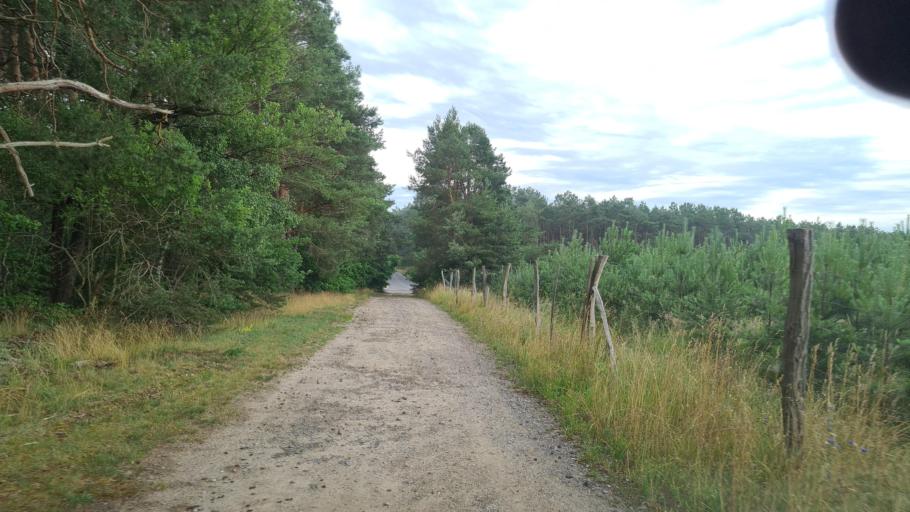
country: DE
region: Brandenburg
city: Sonnewalde
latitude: 51.7289
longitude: 13.6984
